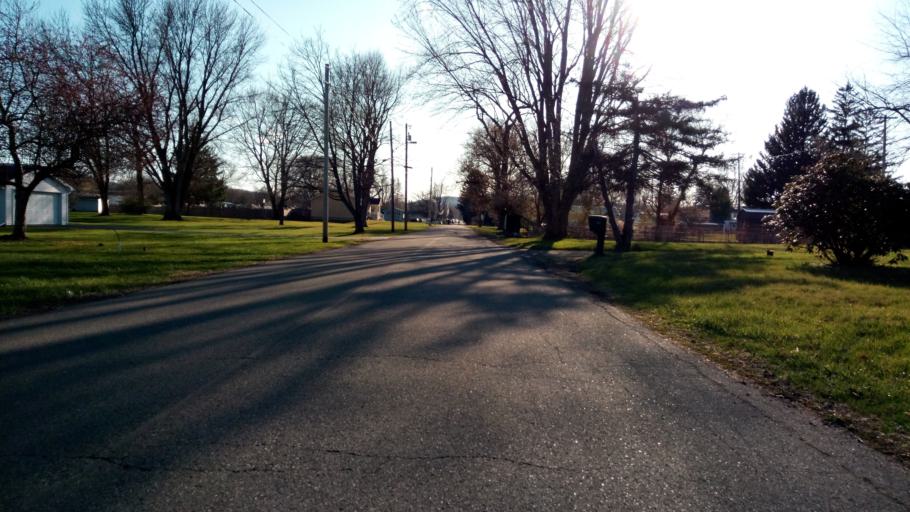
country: US
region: New York
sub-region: Chemung County
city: Elmira
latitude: 42.0778
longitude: -76.7793
